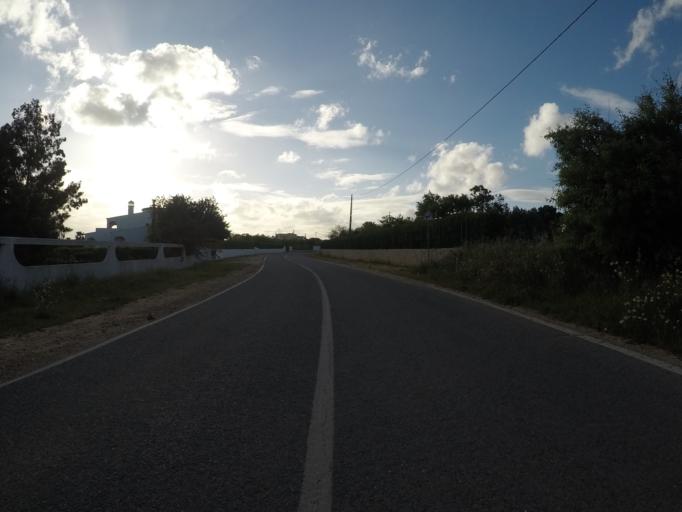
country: PT
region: Faro
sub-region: Lagoa
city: Carvoeiro
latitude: 37.0948
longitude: -8.4351
